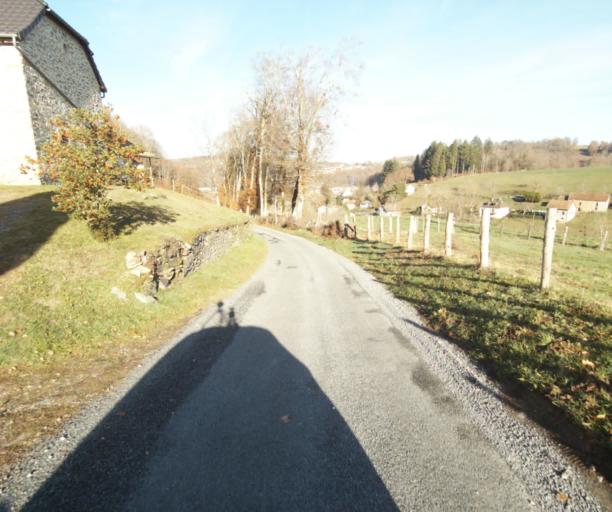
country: FR
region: Limousin
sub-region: Departement de la Correze
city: Laguenne
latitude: 45.2459
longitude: 1.7604
